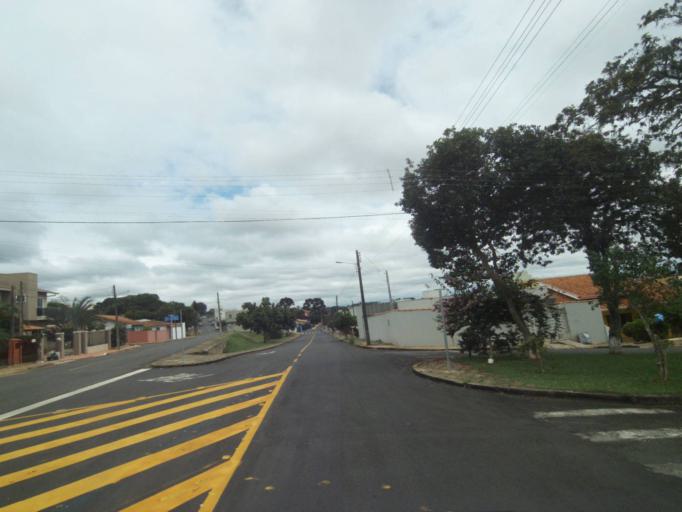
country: BR
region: Parana
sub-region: Telemaco Borba
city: Telemaco Borba
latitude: -24.3371
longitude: -50.6241
